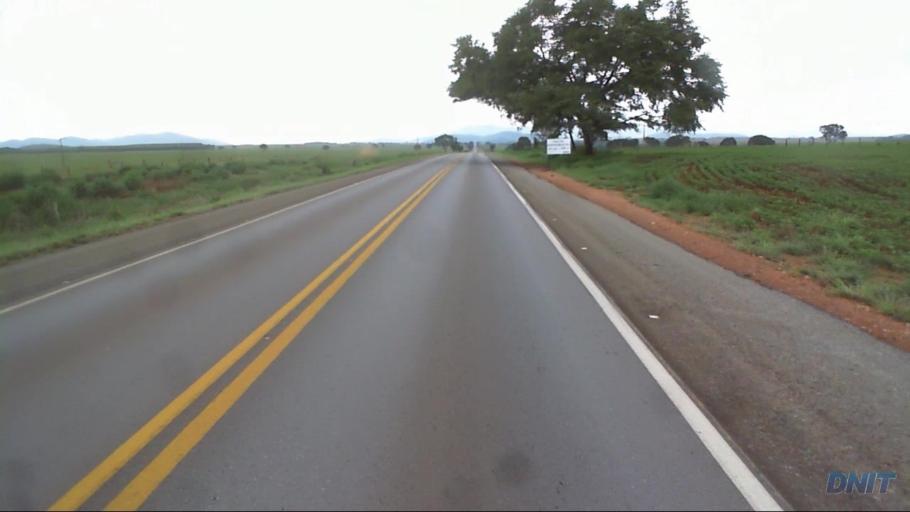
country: BR
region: Goias
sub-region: Barro Alto
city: Barro Alto
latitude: -14.8130
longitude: -49.0429
